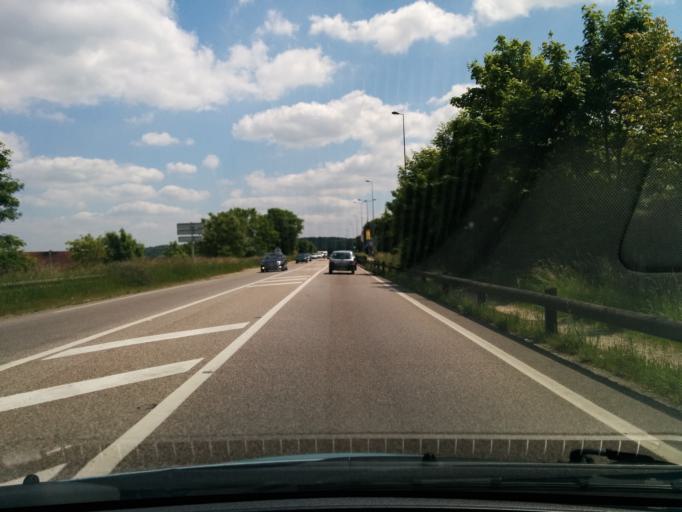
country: FR
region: Ile-de-France
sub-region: Departement des Yvelines
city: Epone
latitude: 48.9594
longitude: 1.8143
